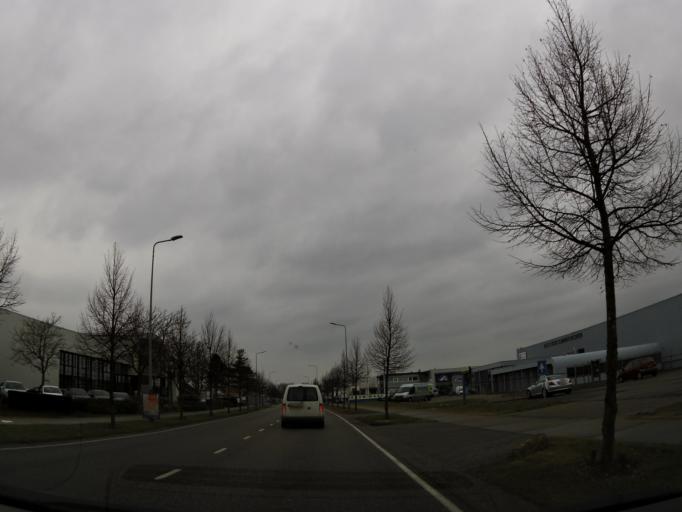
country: NL
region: Limburg
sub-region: Gemeente Sittard-Geleen
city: Sittard
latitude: 51.0149
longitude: 5.8736
